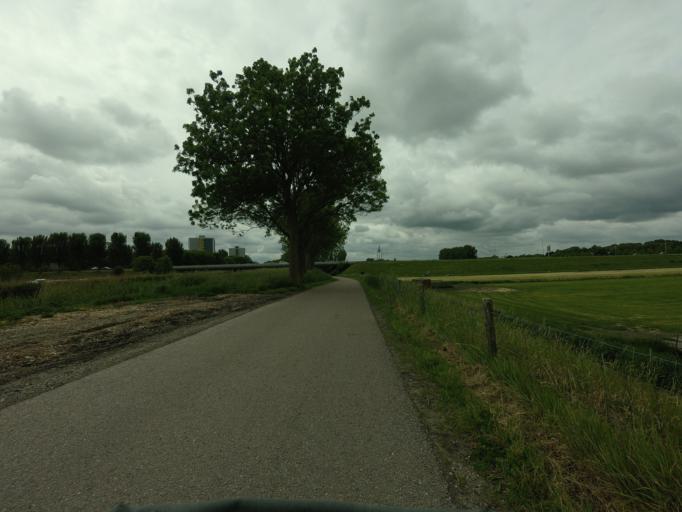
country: NL
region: North Holland
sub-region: Gemeente Purmerend
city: Purmerend
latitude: 52.5303
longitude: 4.9572
